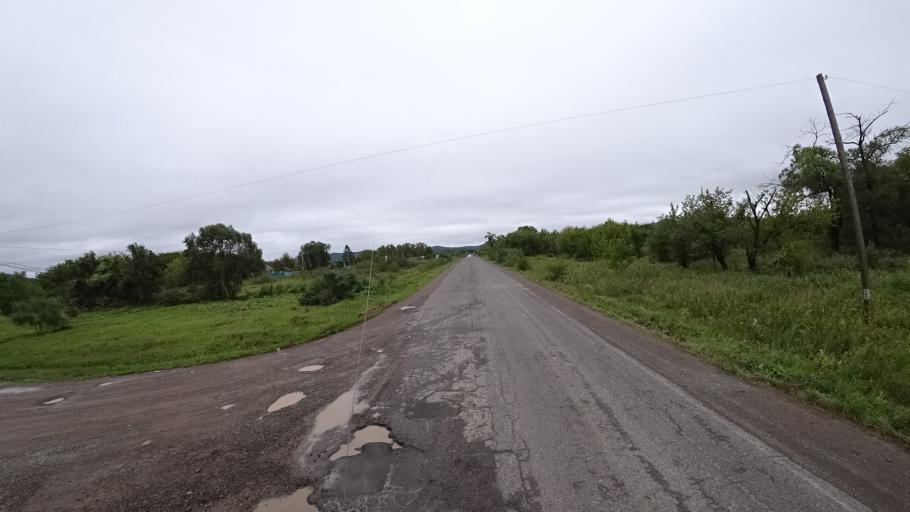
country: RU
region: Primorskiy
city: Monastyrishche
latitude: 44.1945
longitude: 132.4799
